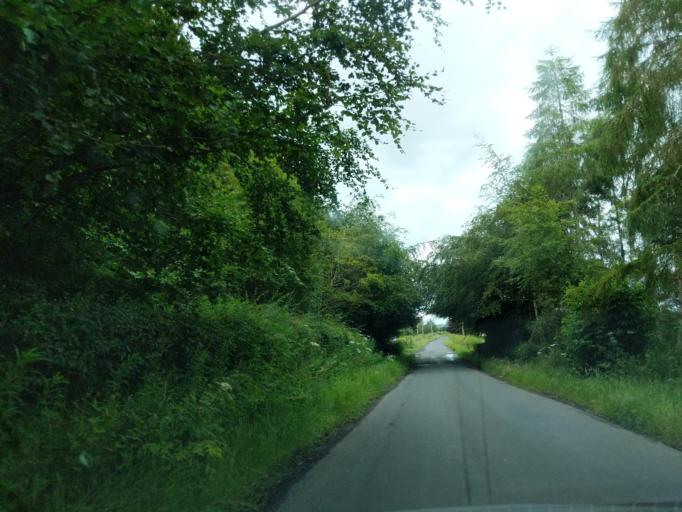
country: GB
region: Scotland
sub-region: South Lanarkshire
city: Dalserf
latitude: 55.7133
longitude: -3.9362
